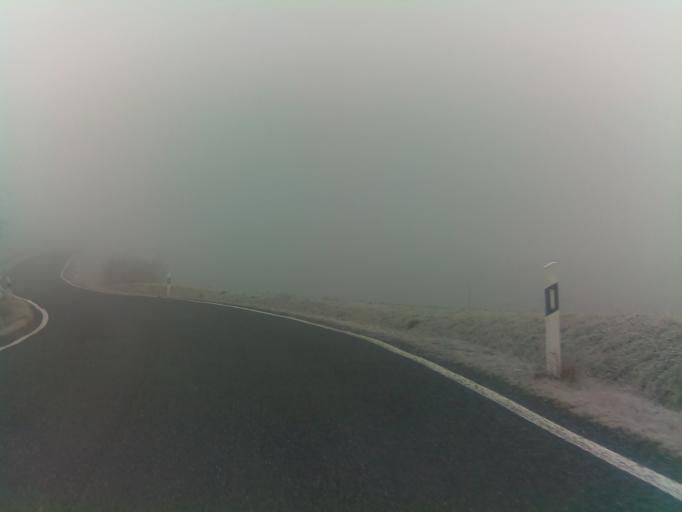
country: DE
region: Bavaria
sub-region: Regierungsbezirk Unterfranken
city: Donnersdorf
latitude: 49.9452
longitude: 10.4354
